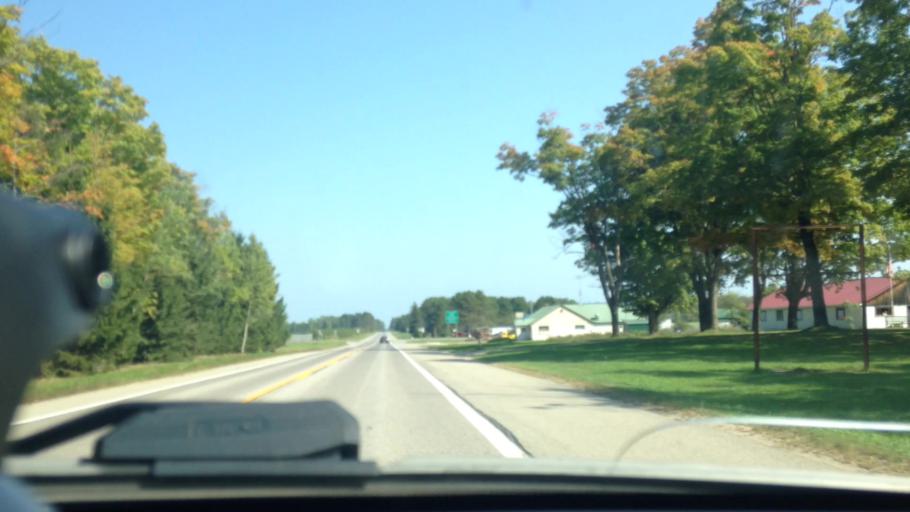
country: US
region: Michigan
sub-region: Luce County
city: Newberry
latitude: 46.3035
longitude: -85.4608
